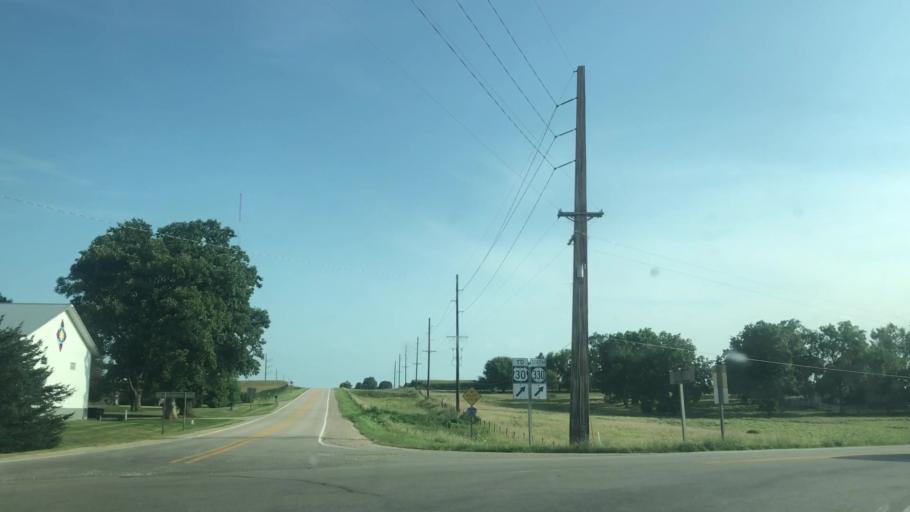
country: US
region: Iowa
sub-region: Marshall County
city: Marshalltown
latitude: 42.0261
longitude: -93.0001
